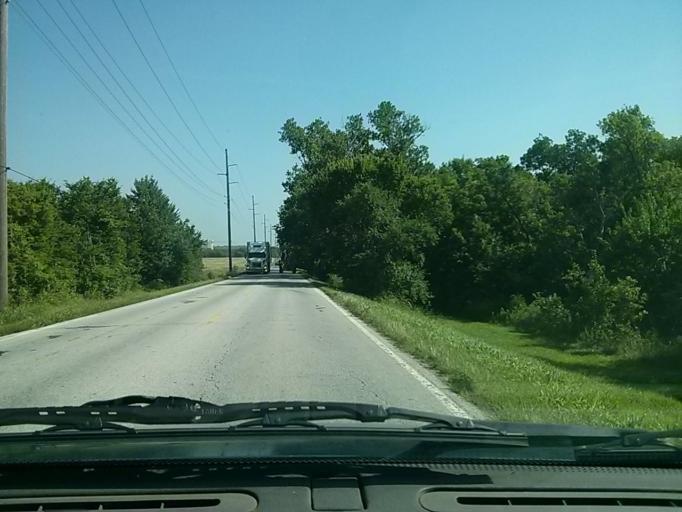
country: US
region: Oklahoma
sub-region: Rogers County
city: Catoosa
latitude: 36.1432
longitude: -95.7617
